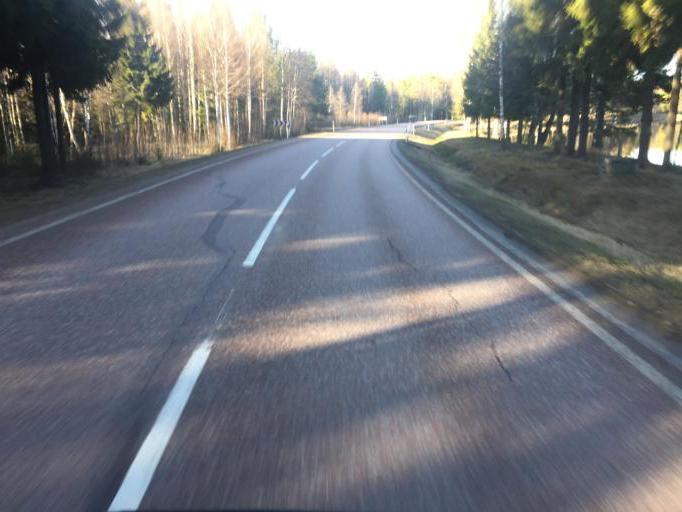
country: SE
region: Dalarna
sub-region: Vansbro Kommun
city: Jarna
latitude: 60.4598
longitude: 14.5768
